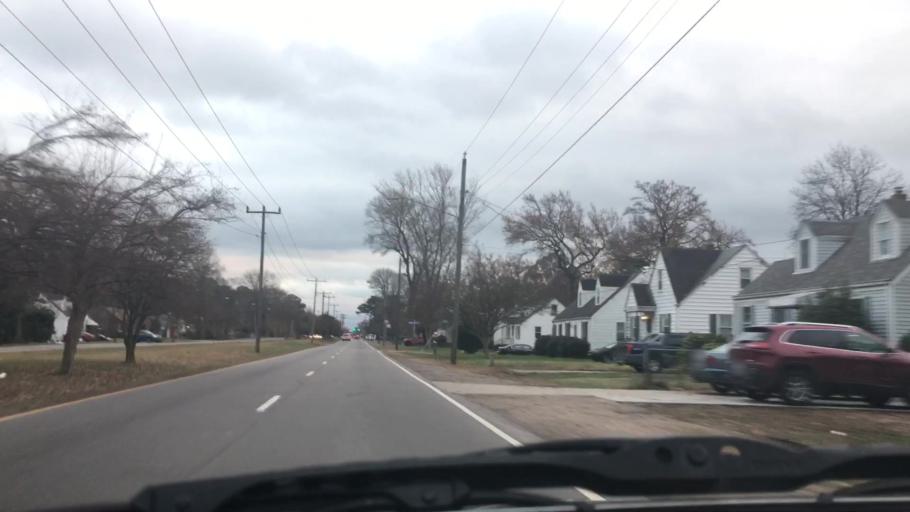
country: US
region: Virginia
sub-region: City of Norfolk
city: Norfolk
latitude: 36.9209
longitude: -76.2426
